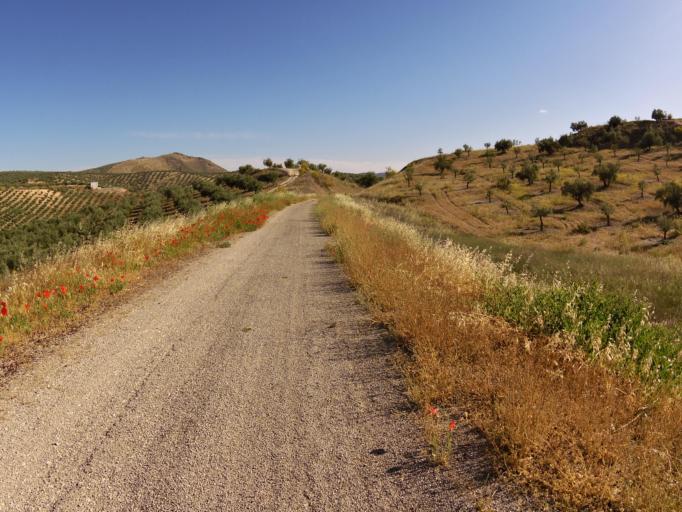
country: ES
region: Andalusia
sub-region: Province of Cordoba
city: Fuente-Tojar
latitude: 37.5833
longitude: -4.1765
